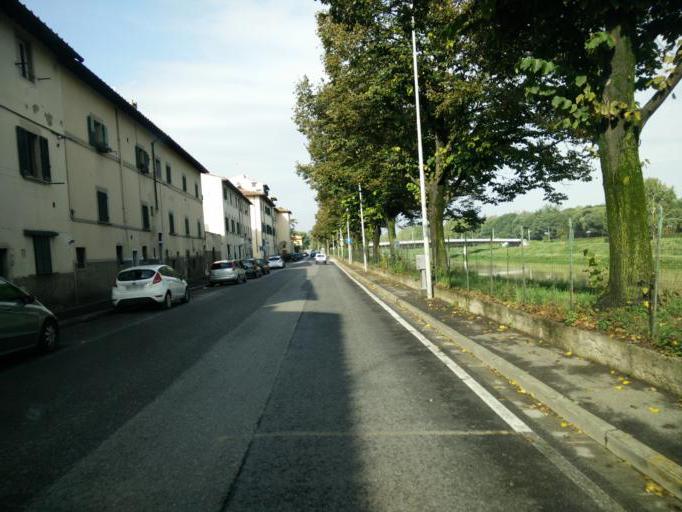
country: IT
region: Tuscany
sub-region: Province of Florence
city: Florence
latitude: 43.7745
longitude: 11.2331
